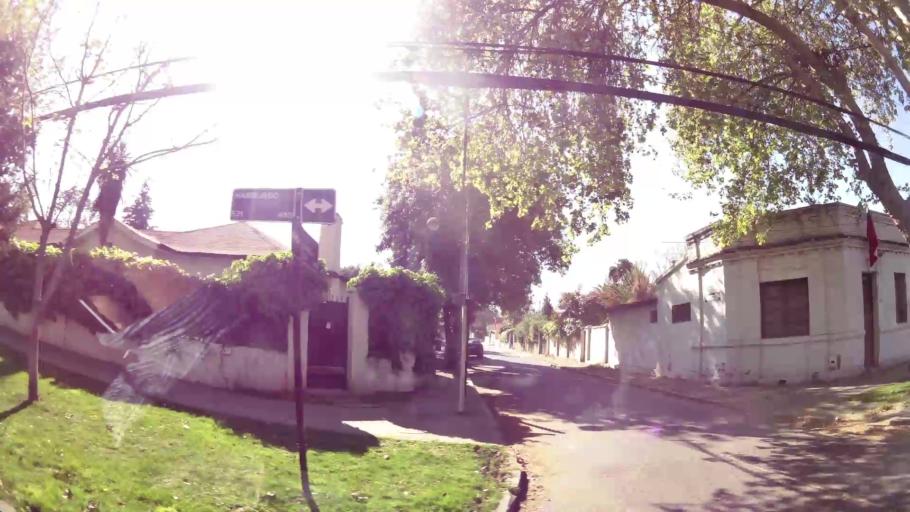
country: CL
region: Santiago Metropolitan
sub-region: Provincia de Santiago
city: Villa Presidente Frei, Nunoa, Santiago, Chile
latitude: -33.4499
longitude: -70.5766
